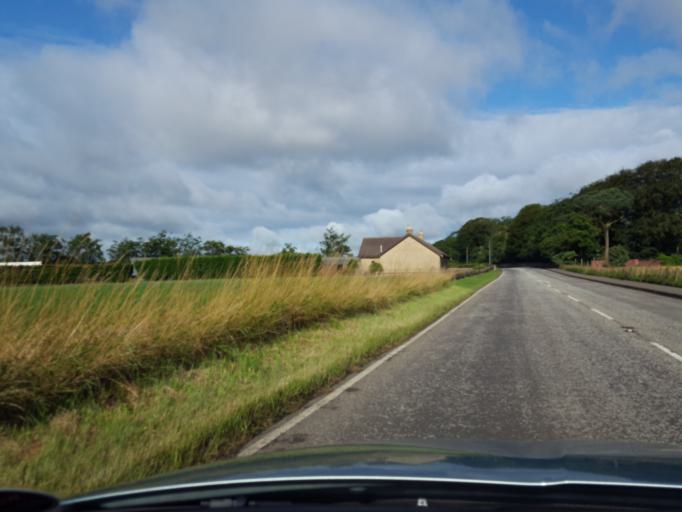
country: GB
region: Scotland
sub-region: West Lothian
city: Linlithgow
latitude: 55.9695
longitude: -3.5394
